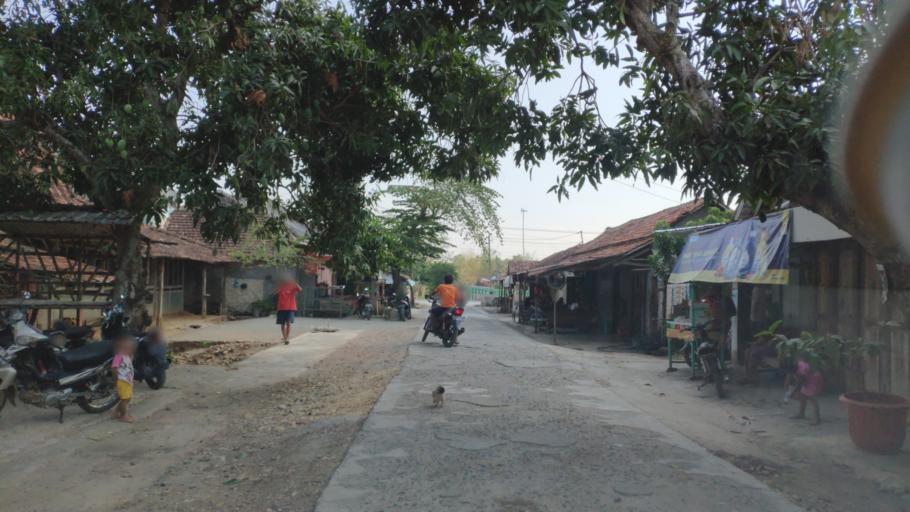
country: ID
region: Central Java
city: Ngapus
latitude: -6.9543
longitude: 111.1509
